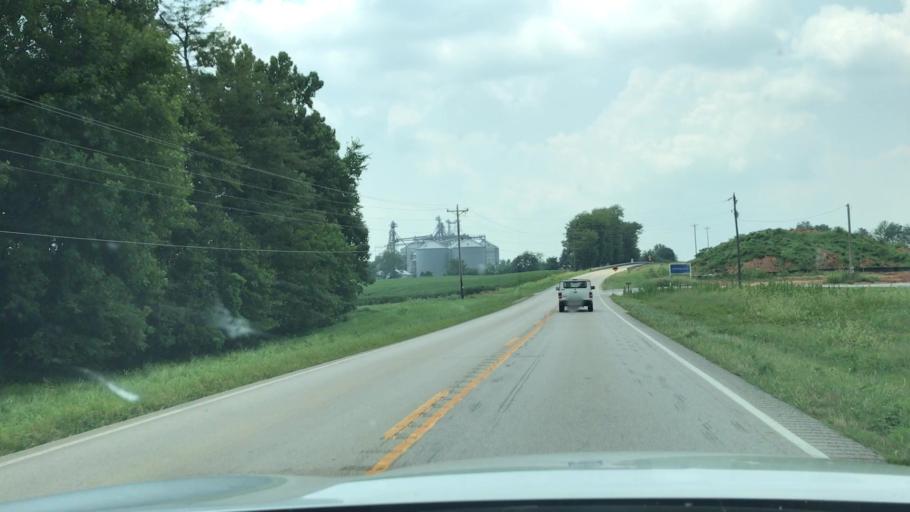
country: US
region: Kentucky
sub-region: Todd County
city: Guthrie
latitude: 36.6599
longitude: -87.1723
